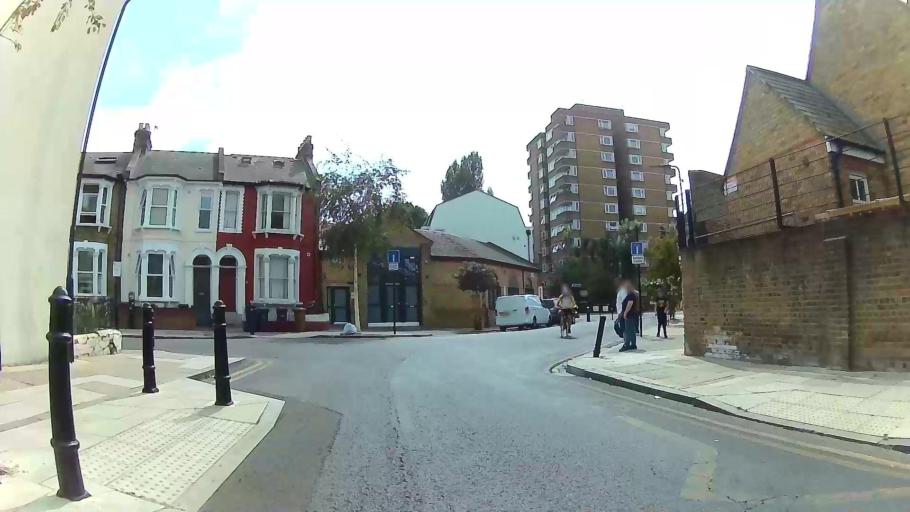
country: GB
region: England
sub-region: Greater London
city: Islington
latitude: 51.5521
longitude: -0.0791
